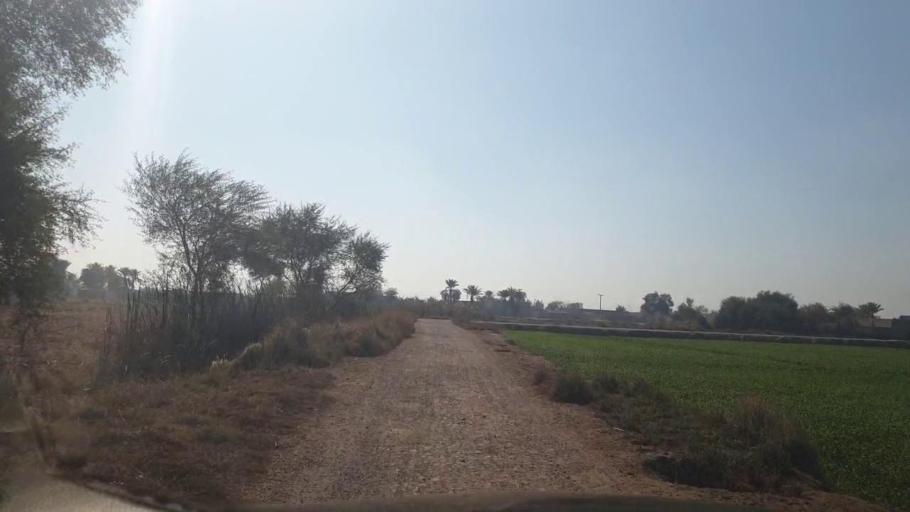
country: PK
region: Sindh
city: Ghotki
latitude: 27.9847
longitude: 69.3558
